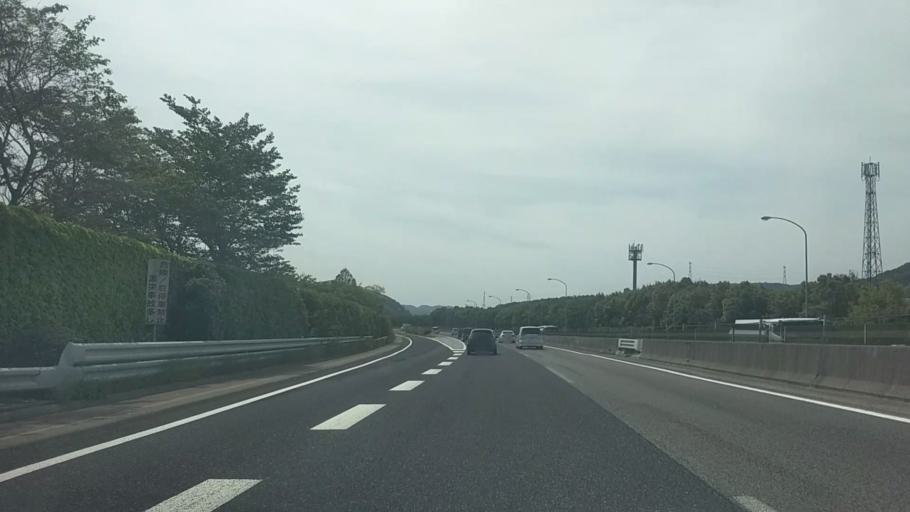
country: JP
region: Aichi
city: Gamagori
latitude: 34.8967
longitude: 137.2574
